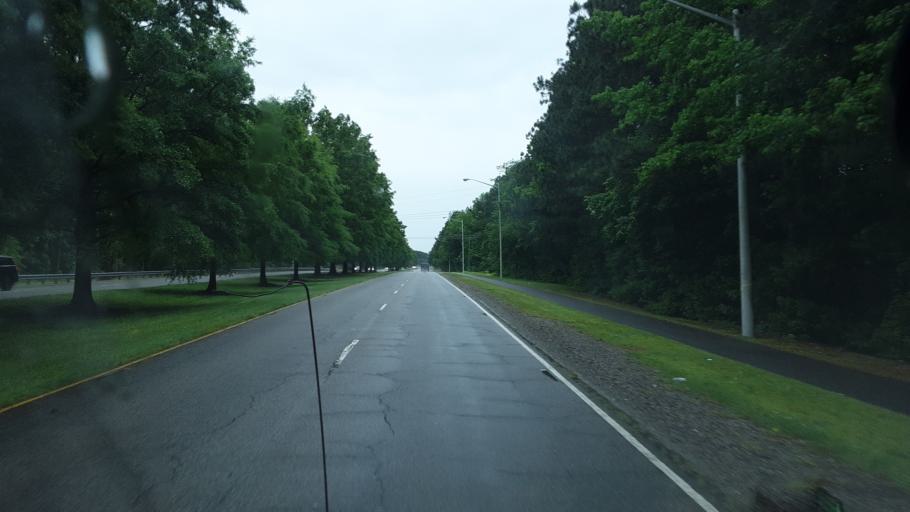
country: US
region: Virginia
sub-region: City of Virginia Beach
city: Virginia Beach
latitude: 36.8019
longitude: -75.9928
